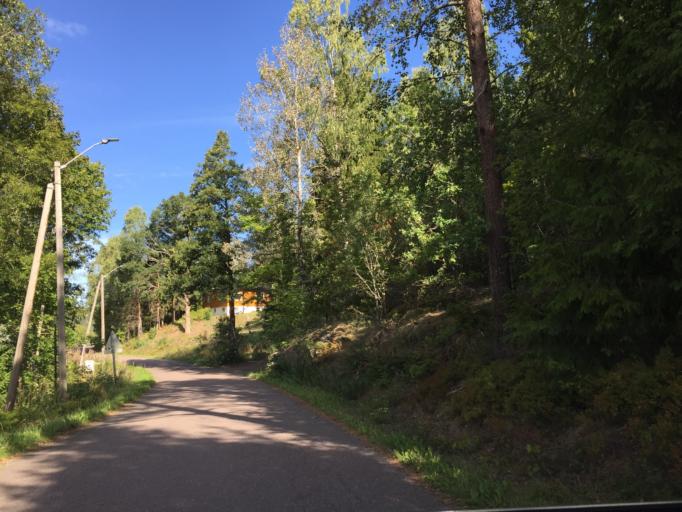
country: NO
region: Vestfold
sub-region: Holmestrand
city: Gullhaug
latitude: 59.4784
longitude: 10.1784
